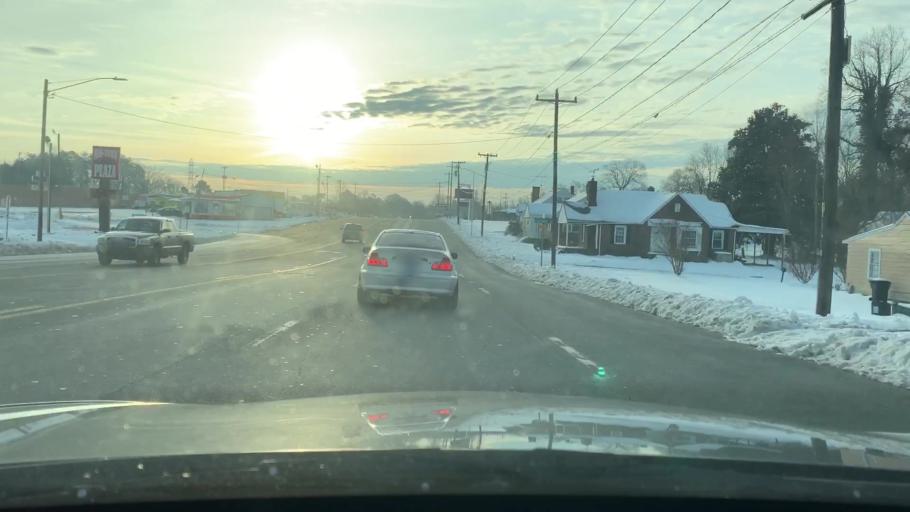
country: US
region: North Carolina
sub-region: Alamance County
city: Burlington
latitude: 36.1000
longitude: -79.4216
